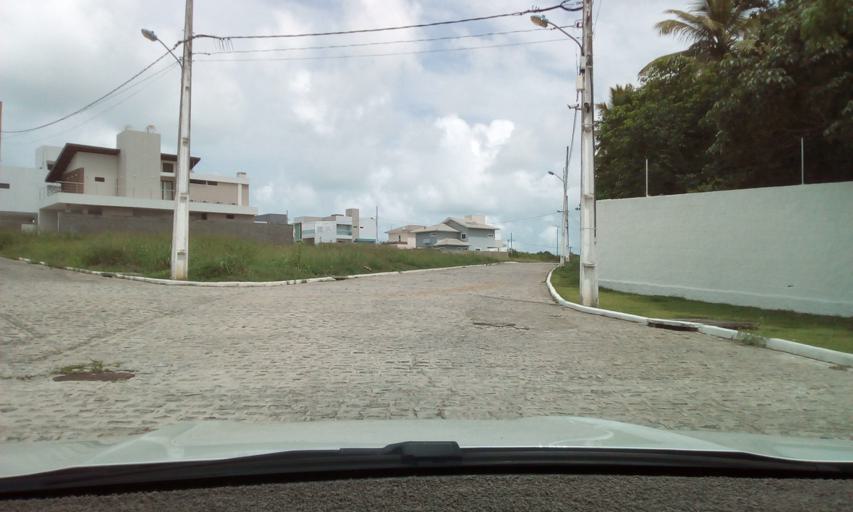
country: BR
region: Paraiba
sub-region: Joao Pessoa
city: Joao Pessoa
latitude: -7.1417
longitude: -34.8292
